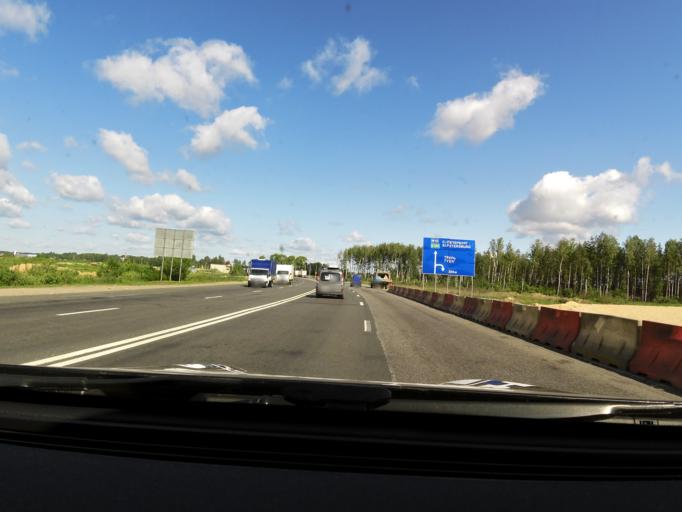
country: RU
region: Tverskaya
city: Tver
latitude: 56.8821
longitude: 35.7822
